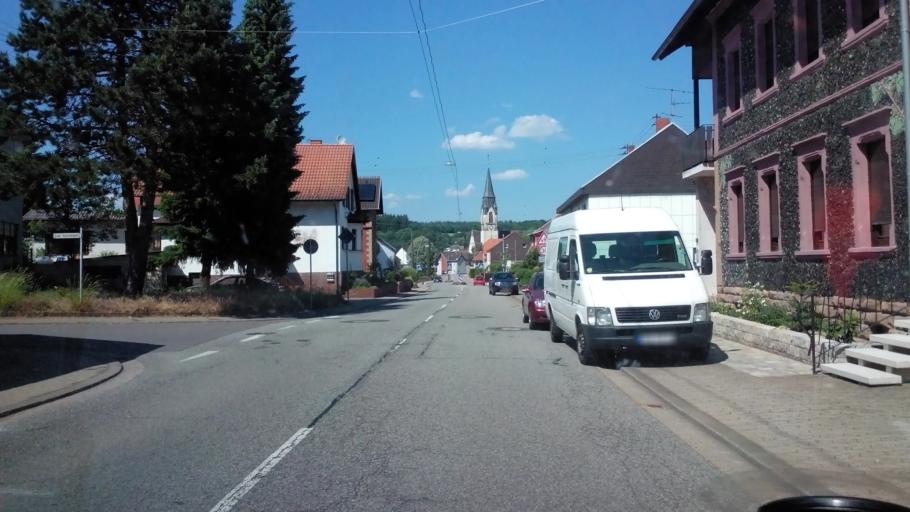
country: DE
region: Saarland
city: Puttlingen
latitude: 49.3308
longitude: 6.8603
